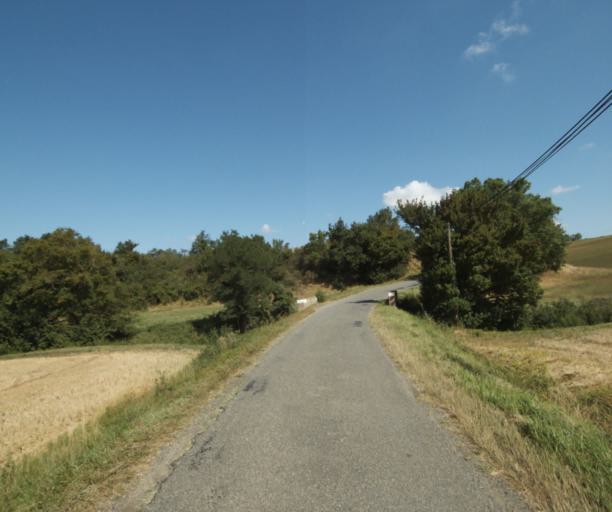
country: FR
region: Midi-Pyrenees
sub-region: Departement de la Haute-Garonne
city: Auriac-sur-Vendinelle
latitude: 43.4569
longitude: 1.7870
